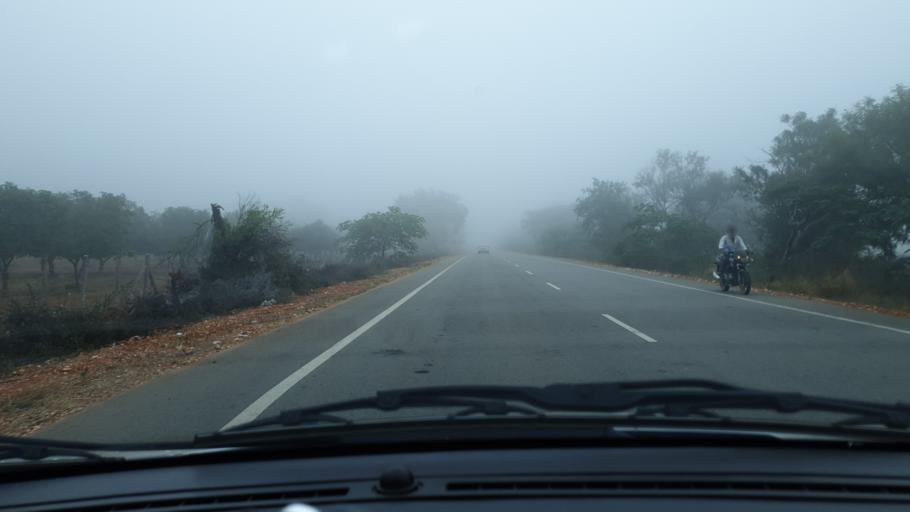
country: IN
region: Telangana
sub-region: Mahbubnagar
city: Nagar Karnul
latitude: 16.6405
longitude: 78.5931
